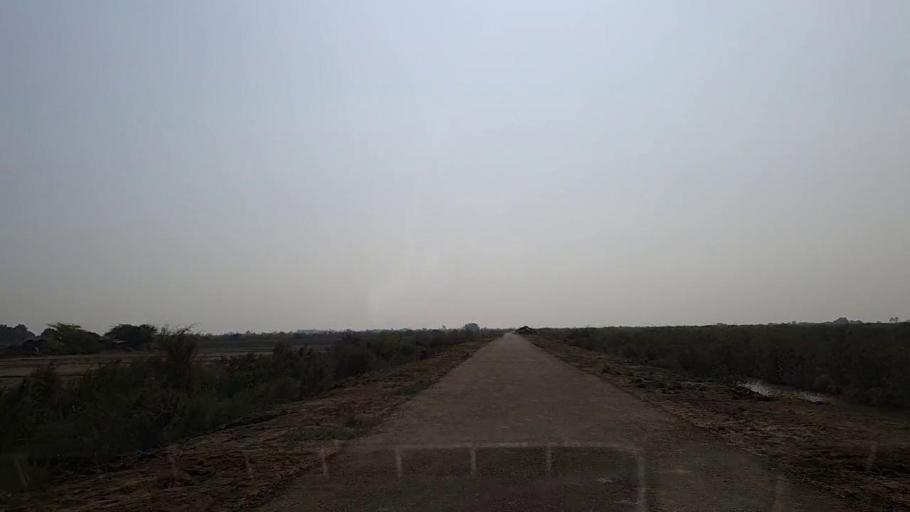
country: PK
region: Sindh
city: Mirpur Sakro
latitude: 24.6588
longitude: 67.6925
